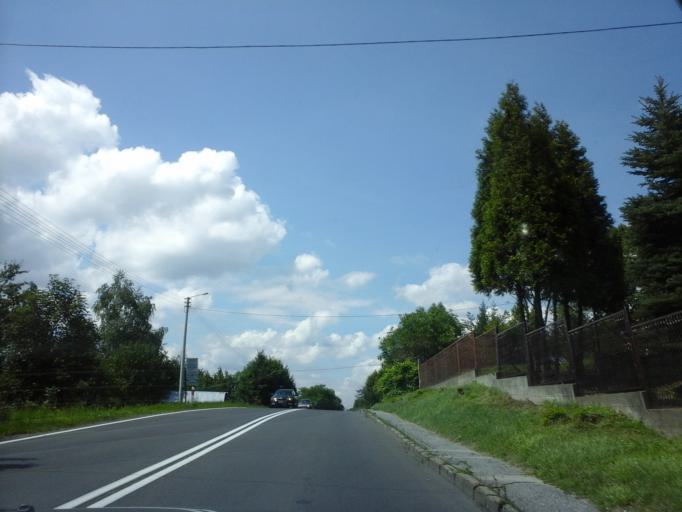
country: PL
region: Lesser Poland Voivodeship
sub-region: Powiat suski
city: Grzechynia
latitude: 49.7328
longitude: 19.6547
